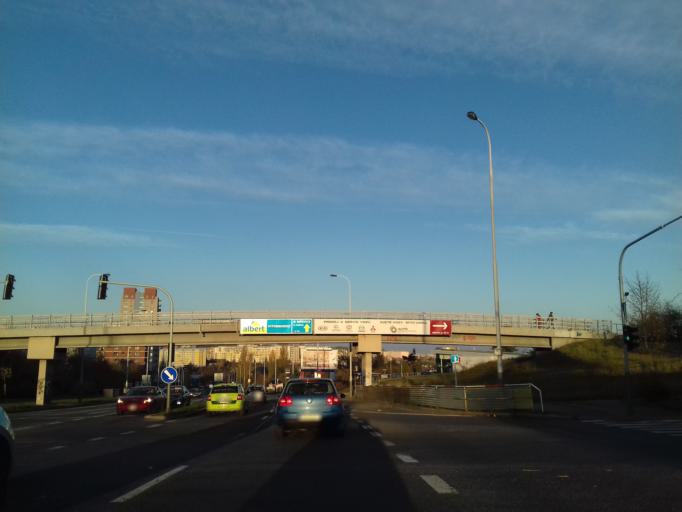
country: CZ
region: Praha
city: Branik
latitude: 50.0410
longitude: 14.3342
